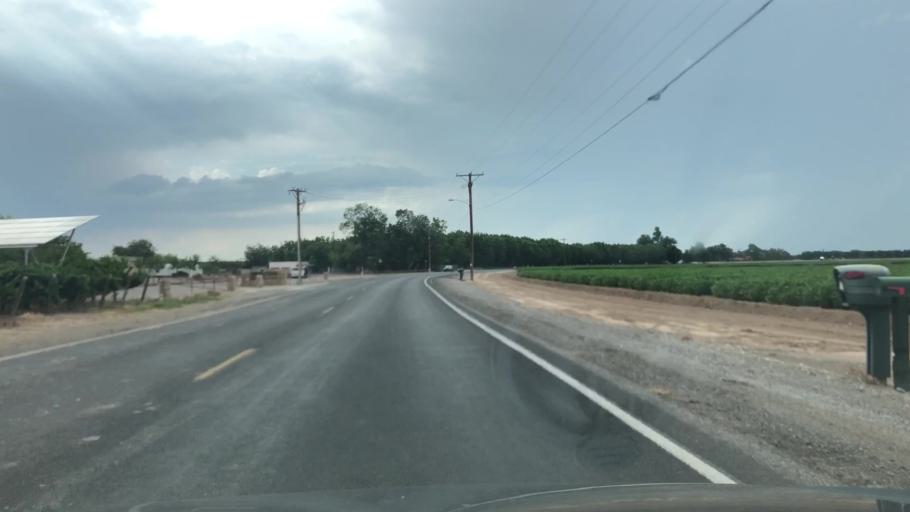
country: US
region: New Mexico
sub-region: Dona Ana County
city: La Union
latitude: 31.9691
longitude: -106.6511
